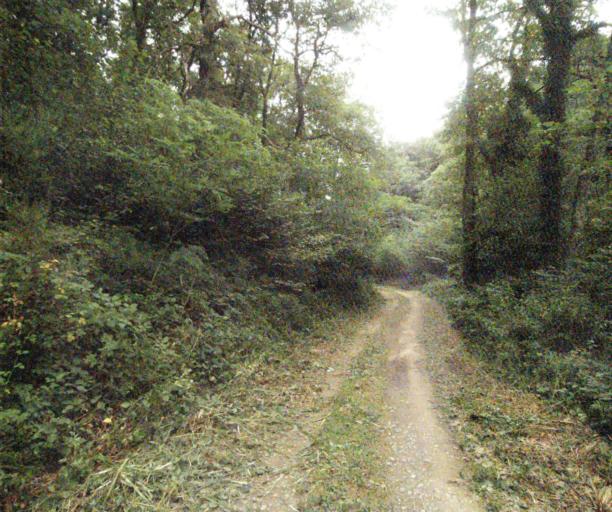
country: FR
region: Midi-Pyrenees
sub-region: Departement du Tarn
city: Soreze
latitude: 43.4179
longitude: 2.0647
